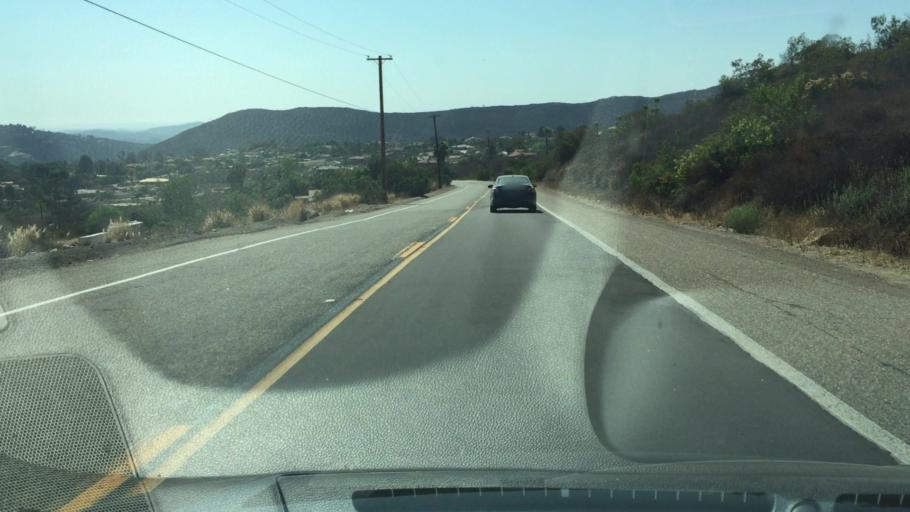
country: US
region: California
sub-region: San Diego County
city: Jamul
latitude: 32.7352
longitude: -116.8416
